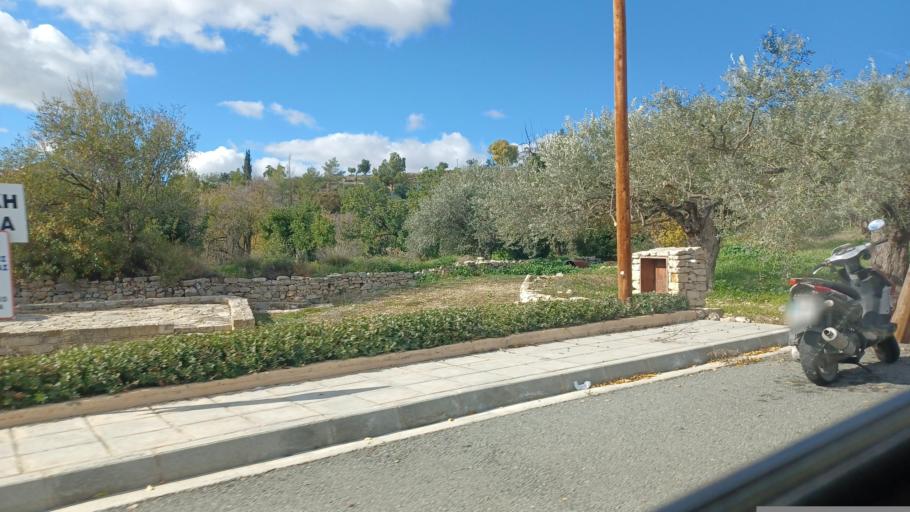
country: CY
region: Limassol
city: Pano Polemidia
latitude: 34.7883
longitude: 32.9767
